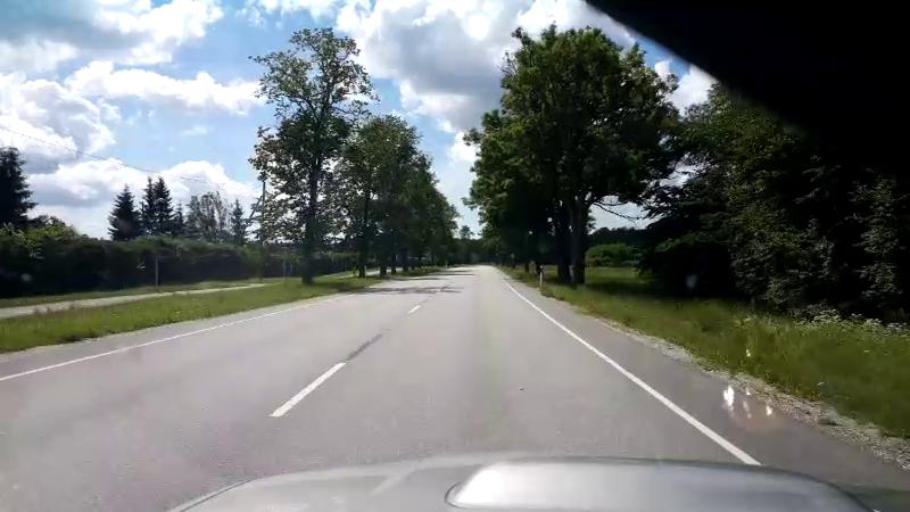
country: EE
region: Jaervamaa
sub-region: Jaerva-Jaani vald
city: Jarva-Jaani
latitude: 59.0374
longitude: 25.7077
